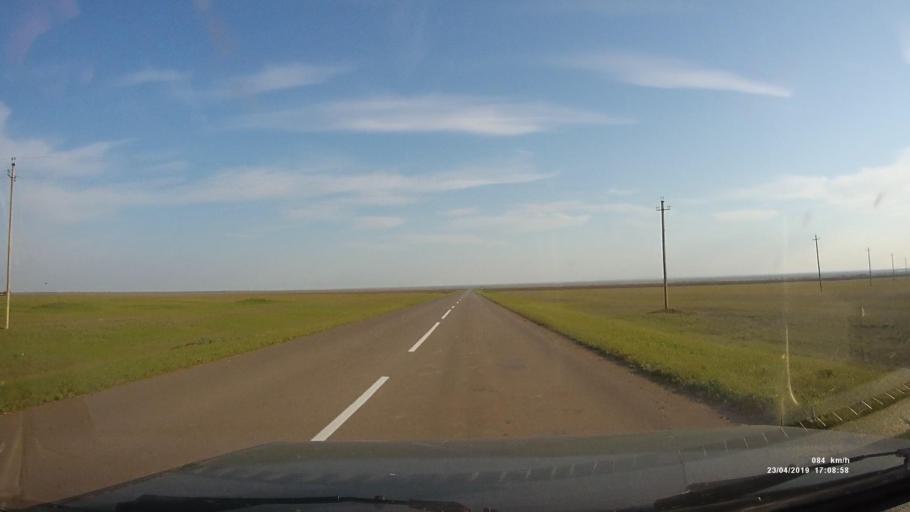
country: RU
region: Kalmykiya
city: Priyutnoye
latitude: 46.2650
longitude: 43.4844
